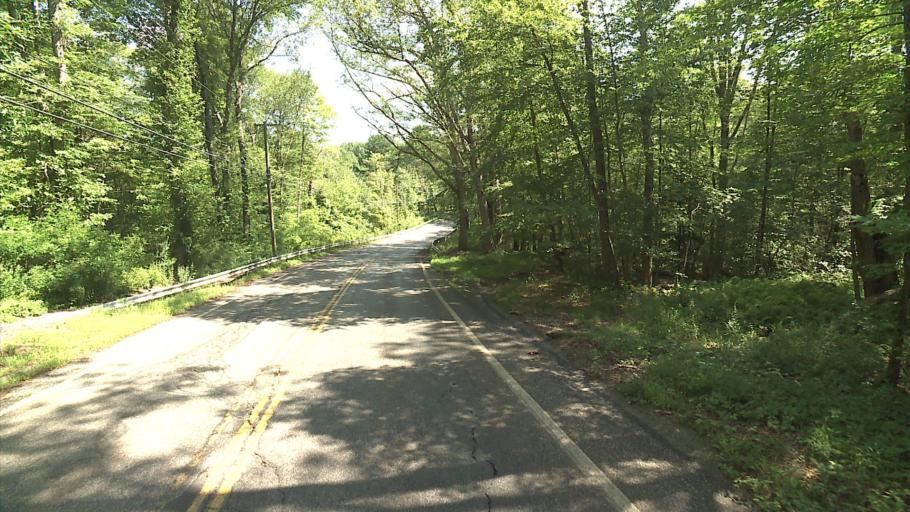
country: US
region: Connecticut
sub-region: Tolland County
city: Stafford
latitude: 41.9195
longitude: -72.1803
